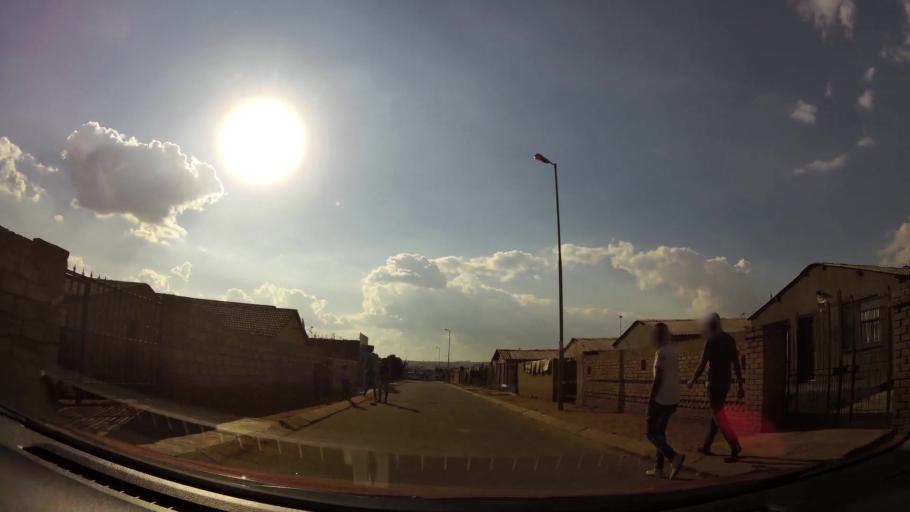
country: ZA
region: Gauteng
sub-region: City of Johannesburg Metropolitan Municipality
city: Soweto
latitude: -26.2321
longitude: 27.8700
